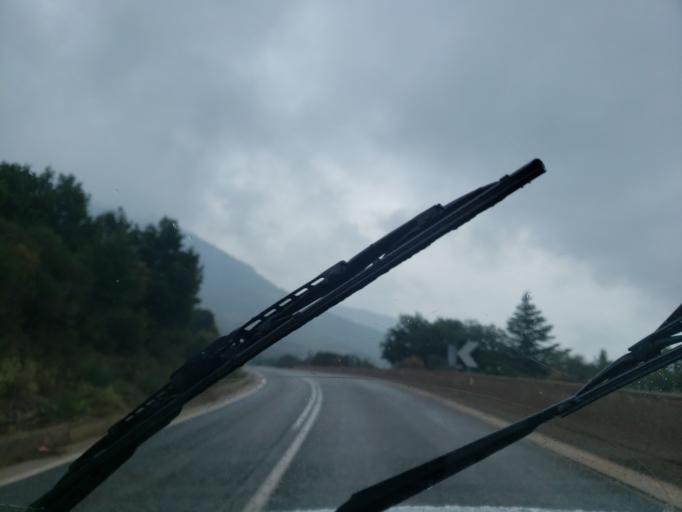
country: GR
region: Central Greece
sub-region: Nomos Fokidos
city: Amfissa
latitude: 38.5899
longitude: 22.3856
